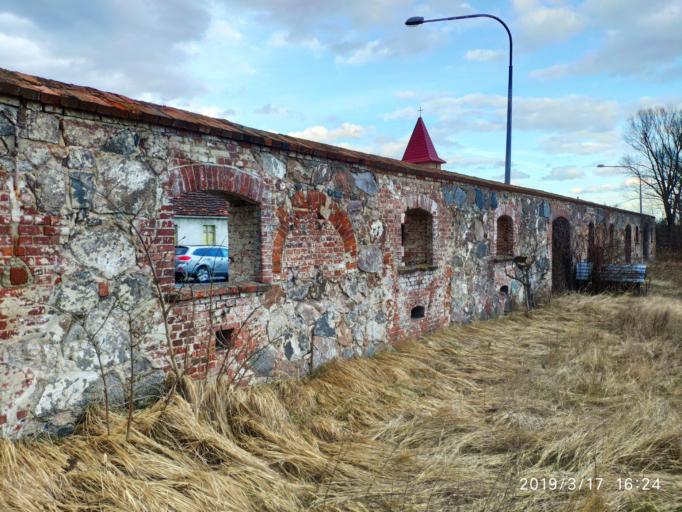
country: PL
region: Lubusz
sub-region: Powiat zielonogorski
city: Zabor
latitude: 51.9323
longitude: 15.6129
